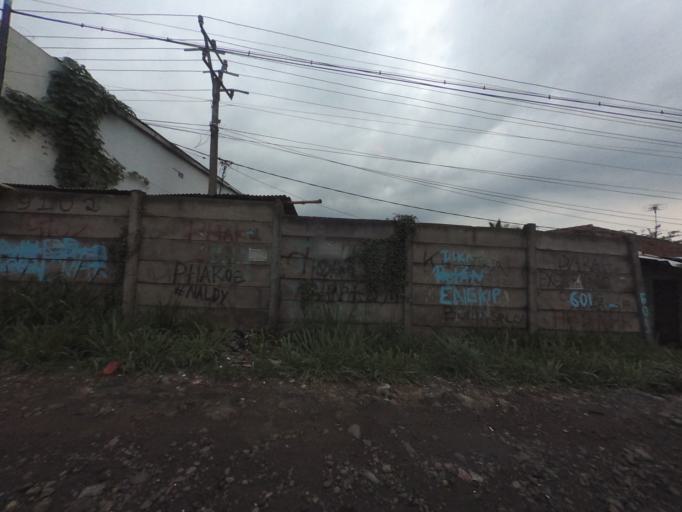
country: ID
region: West Java
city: Cicurug
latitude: -6.8407
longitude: 106.7614
